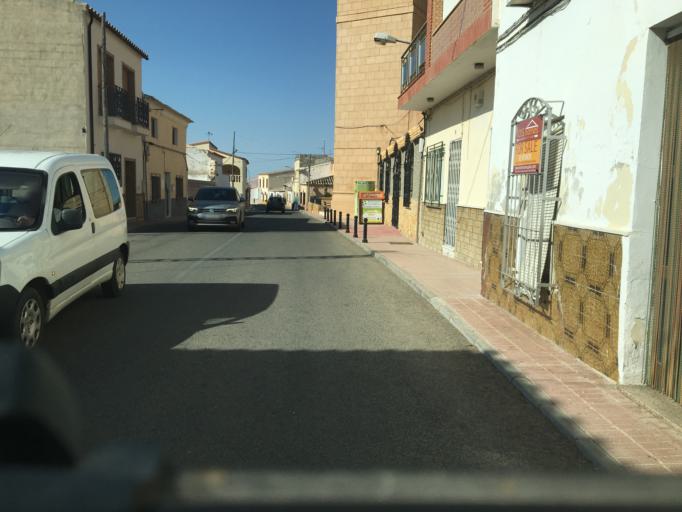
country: ES
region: Andalusia
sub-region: Provincia de Almeria
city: Huercal-Overa
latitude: 37.4624
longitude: -1.9889
